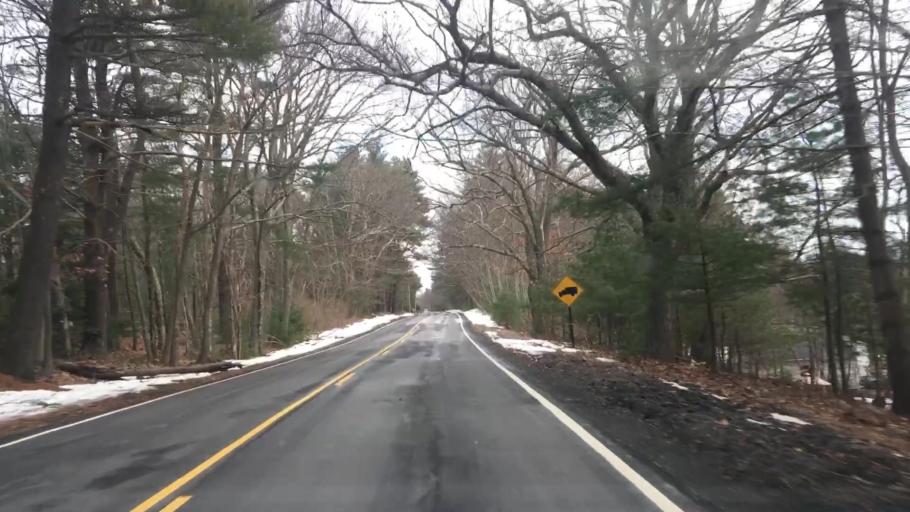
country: US
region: Maine
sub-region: York County
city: Wells Beach Station
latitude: 43.3264
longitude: -70.6316
